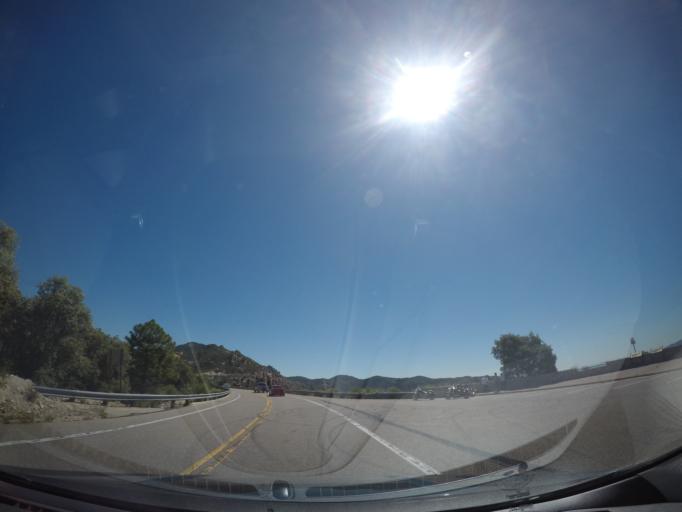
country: US
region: Arizona
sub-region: Pima County
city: Tanque Verde
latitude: 32.3707
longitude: -110.7115
